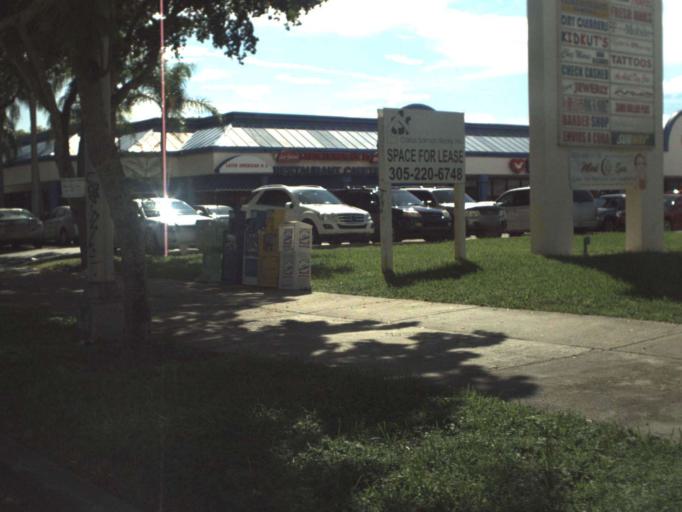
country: US
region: Florida
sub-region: Miami-Dade County
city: Sunset
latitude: 25.7016
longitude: -80.3496
